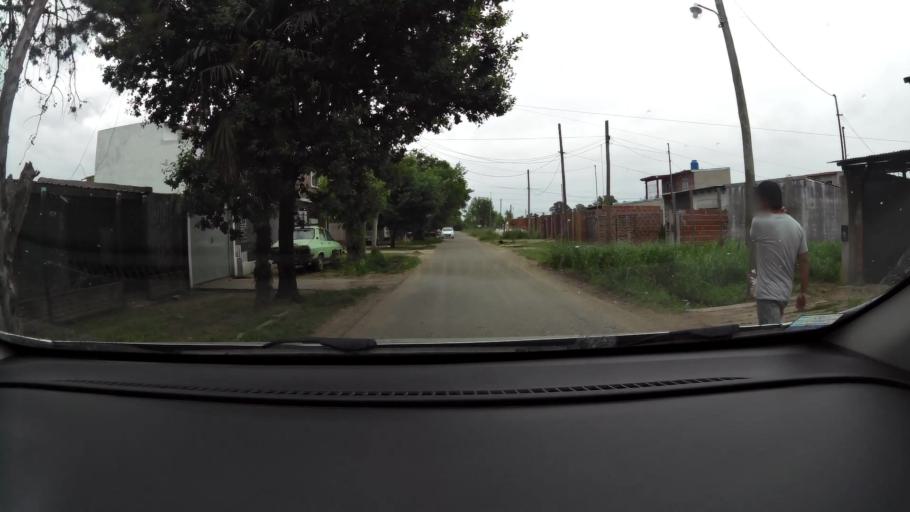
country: AR
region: Buenos Aires
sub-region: Partido de Zarate
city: Zarate
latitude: -34.1127
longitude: -59.0423
